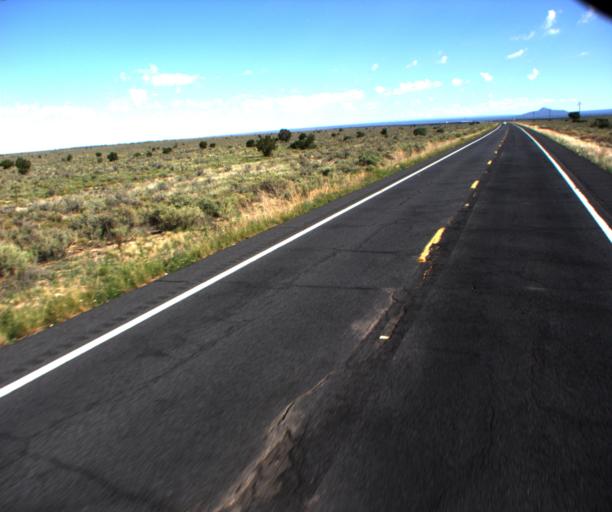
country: US
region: Arizona
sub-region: Coconino County
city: Williams
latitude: 35.6032
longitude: -112.1465
